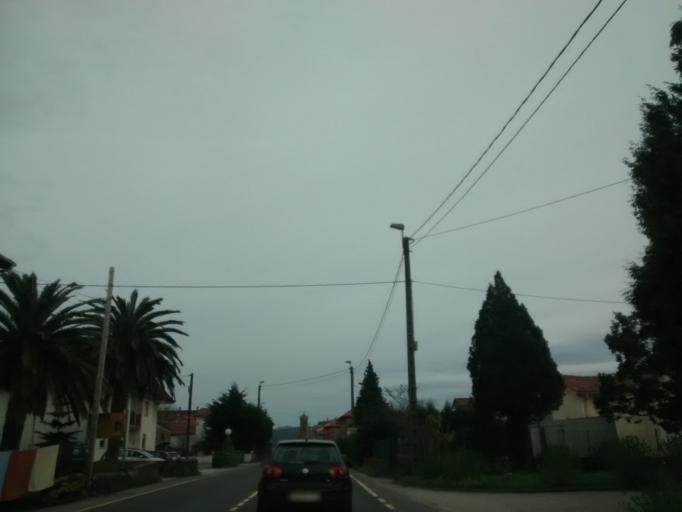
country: ES
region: Cantabria
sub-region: Provincia de Cantabria
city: Puente Viesgo
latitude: 43.3107
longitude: -3.9315
